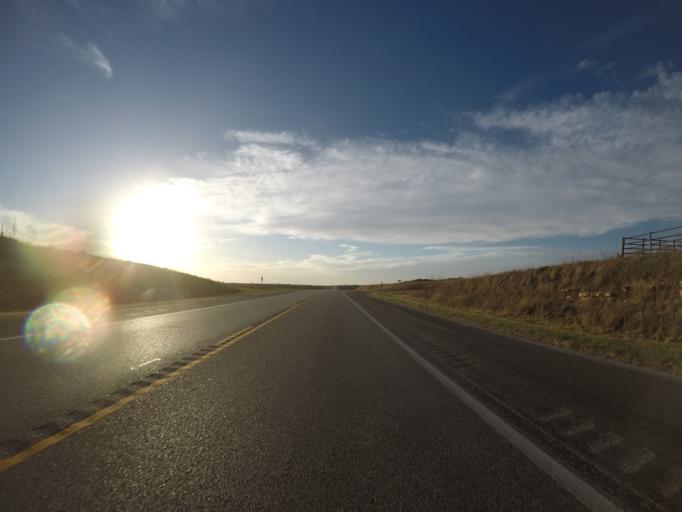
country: US
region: Kansas
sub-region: Chase County
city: Cottonwood Falls
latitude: 38.4055
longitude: -96.4469
